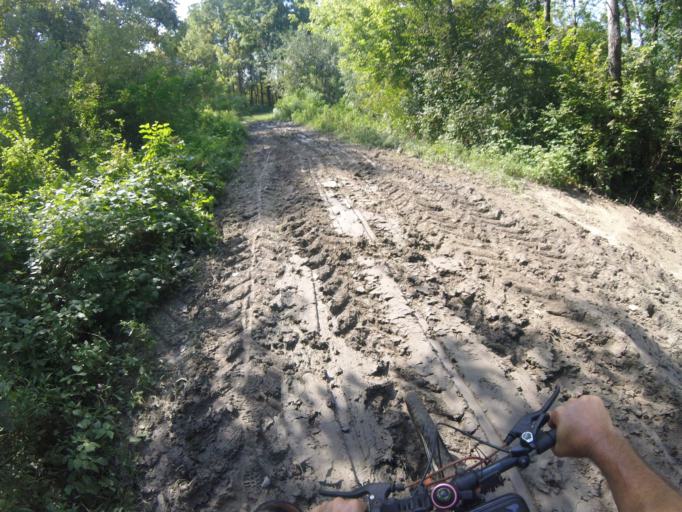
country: HU
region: Bacs-Kiskun
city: Baja
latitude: 46.2097
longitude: 18.8895
